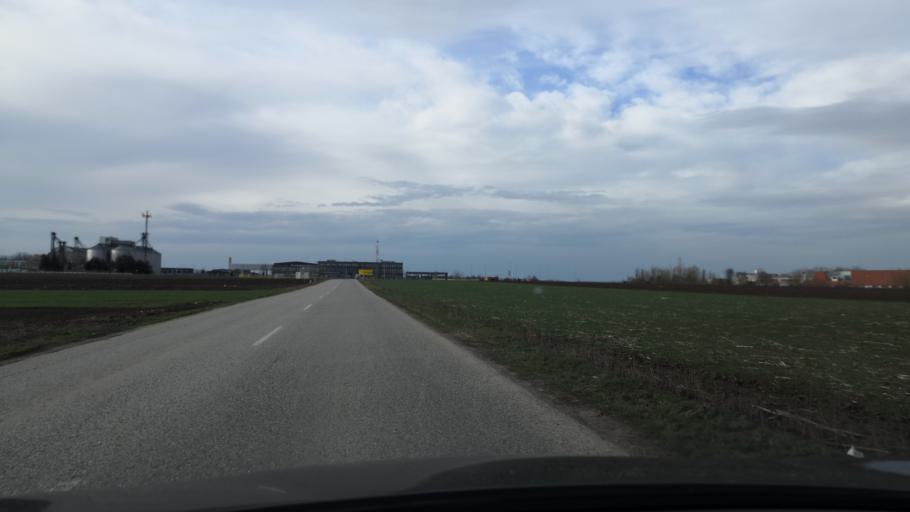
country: RS
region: Autonomna Pokrajina Vojvodina
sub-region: Sremski Okrug
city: Ingija
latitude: 45.0522
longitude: 20.1056
